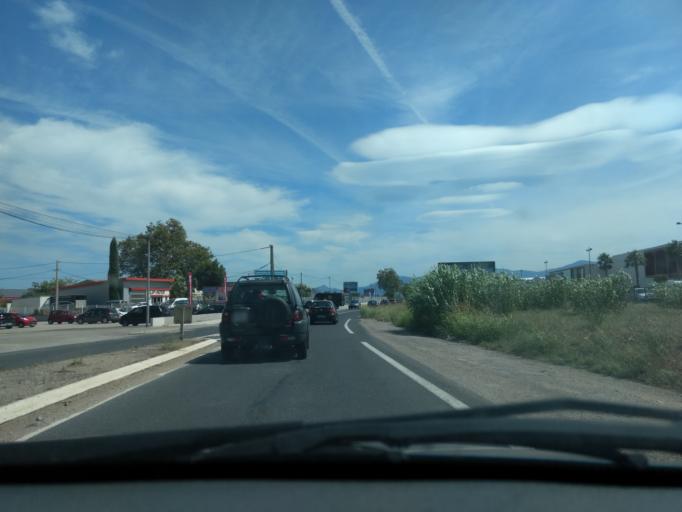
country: FR
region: Languedoc-Roussillon
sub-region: Departement des Pyrenees-Orientales
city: Cabestany
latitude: 42.6696
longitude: 2.9169
